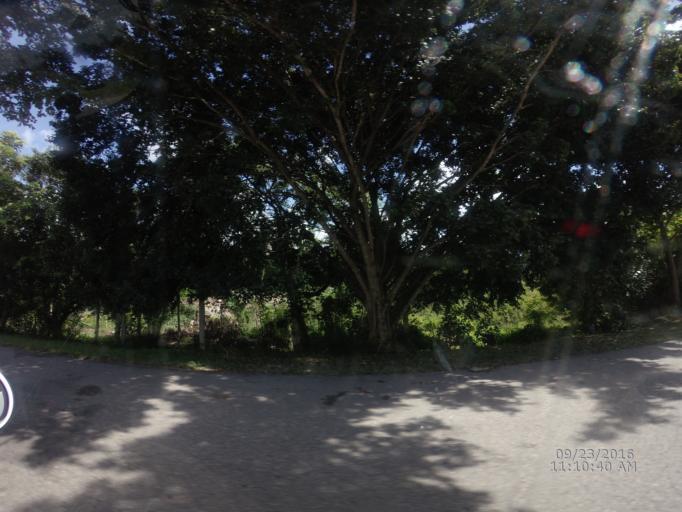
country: CU
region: La Habana
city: Arroyo Naranjo
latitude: 23.0218
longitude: -82.2590
